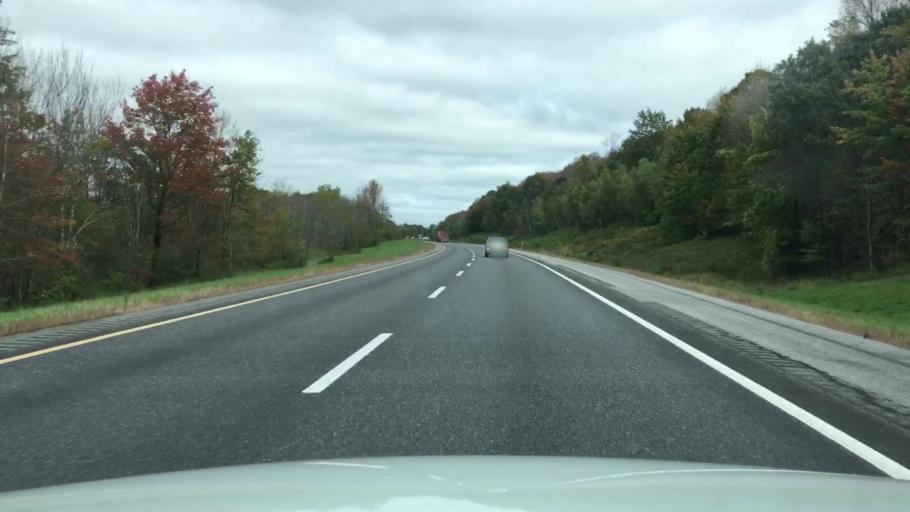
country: US
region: Maine
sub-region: Sagadahoc County
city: Richmond
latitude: 44.0680
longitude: -69.8792
